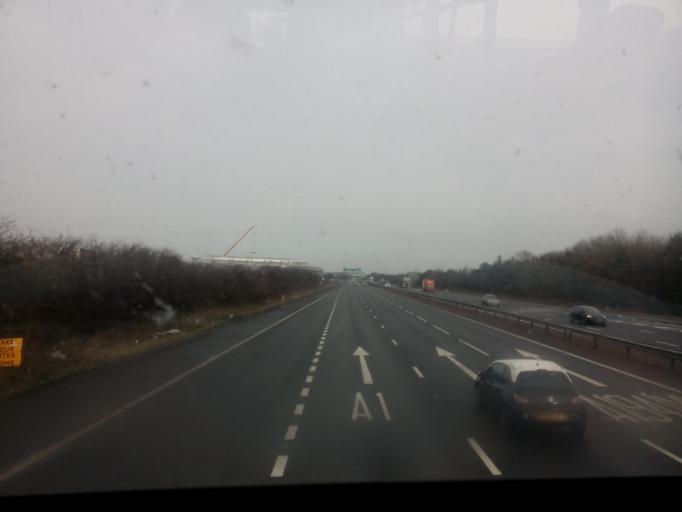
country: GB
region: England
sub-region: County Durham
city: Chester-le-Street
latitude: 54.8919
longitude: -1.5593
